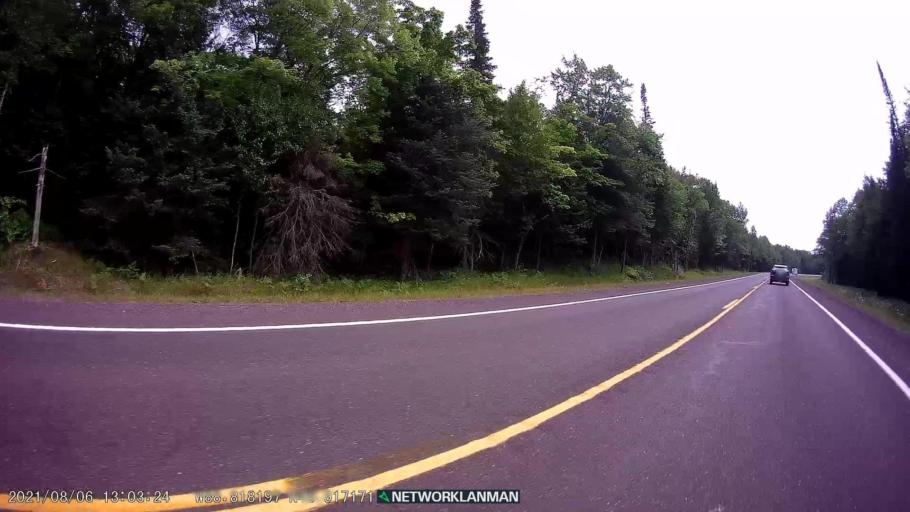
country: US
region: Michigan
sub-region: Houghton County
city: Hancock
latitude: 46.9168
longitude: -88.8186
